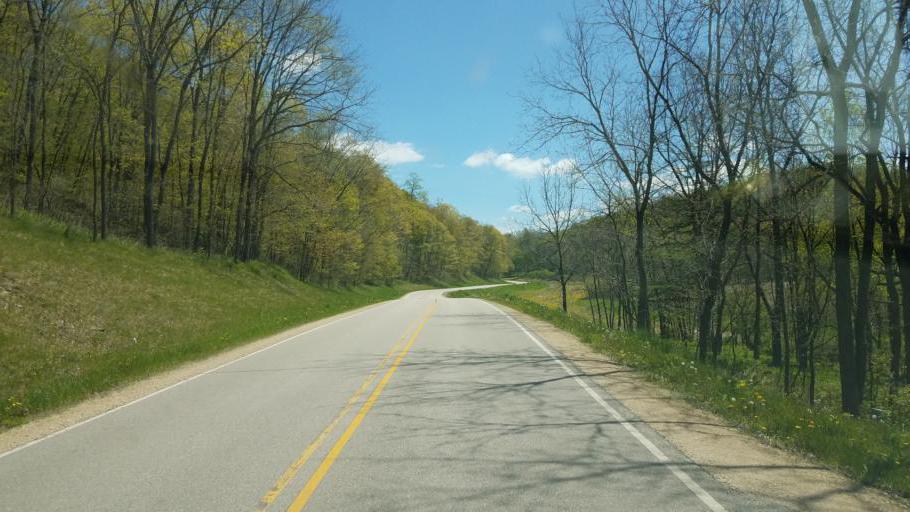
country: US
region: Wisconsin
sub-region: Vernon County
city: Hillsboro
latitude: 43.6432
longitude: -90.4706
